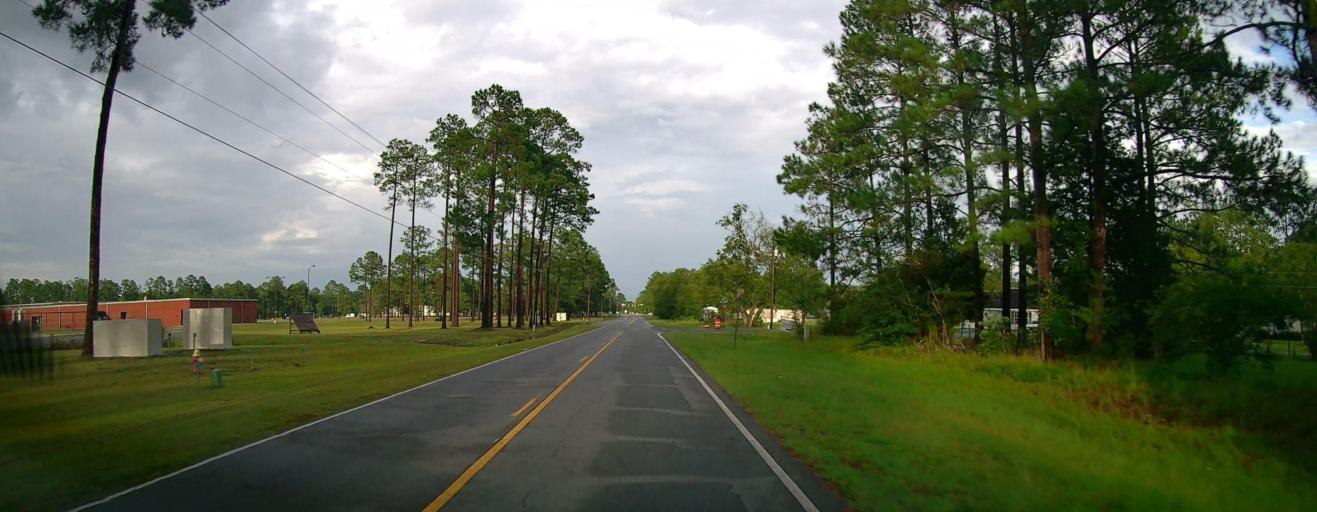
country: US
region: Georgia
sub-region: Ware County
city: Deenwood
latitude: 31.1952
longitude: -82.3891
